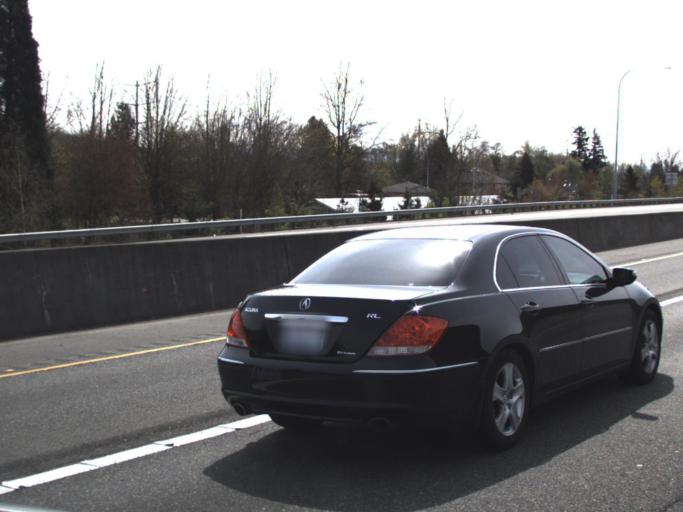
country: US
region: Washington
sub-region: King County
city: Kent
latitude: 47.3841
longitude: -122.2447
